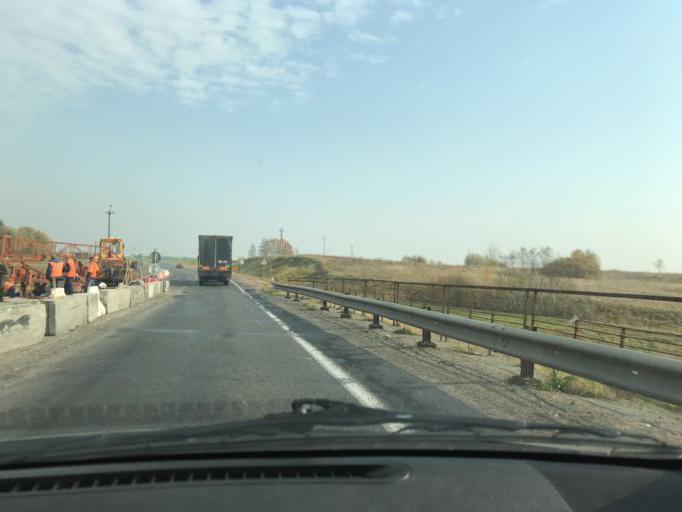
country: BY
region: Vitebsk
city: Chashniki
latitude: 55.0073
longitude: 29.1522
